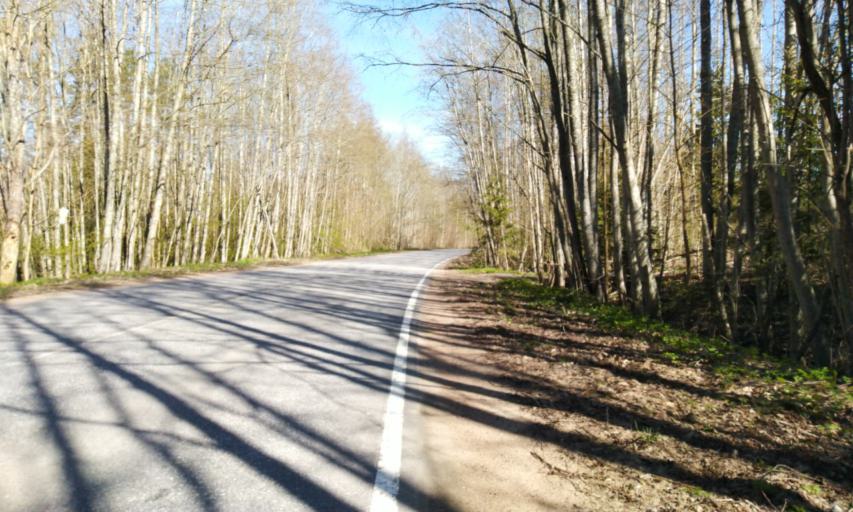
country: RU
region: Leningrad
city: Garbolovo
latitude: 60.4116
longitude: 30.4581
